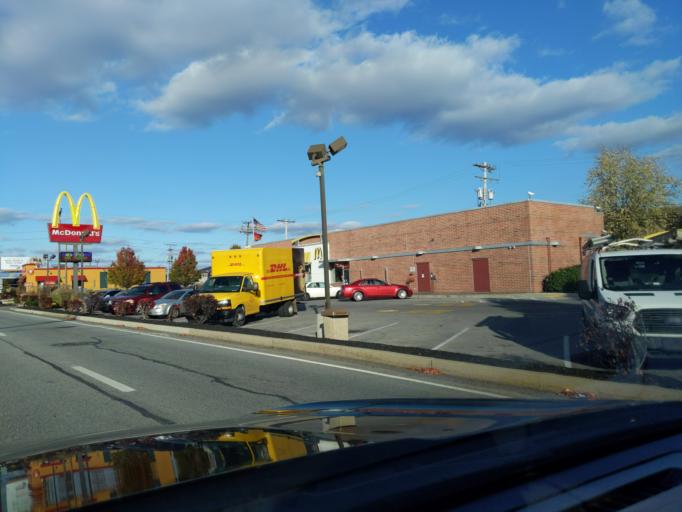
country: US
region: Pennsylvania
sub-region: Blair County
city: Lakemont
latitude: 40.4795
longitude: -78.4029
